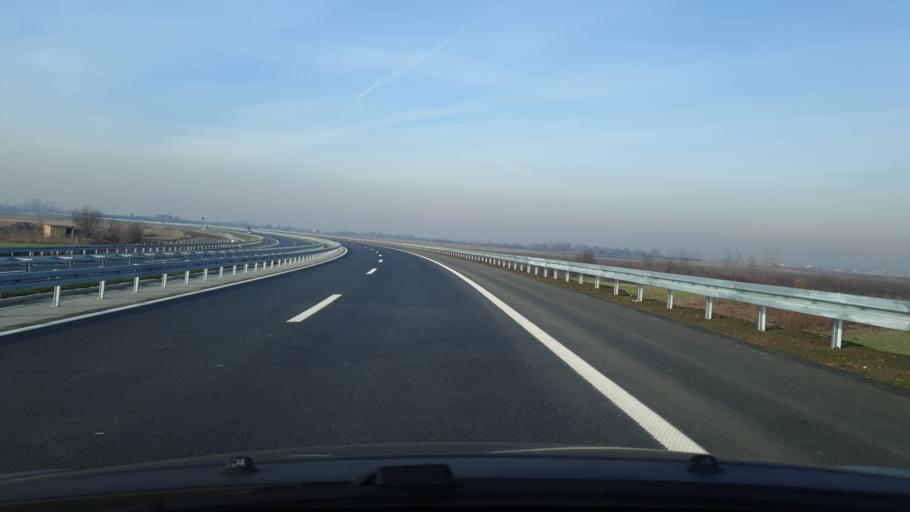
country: RS
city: Boljevci
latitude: 44.7214
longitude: 20.2576
